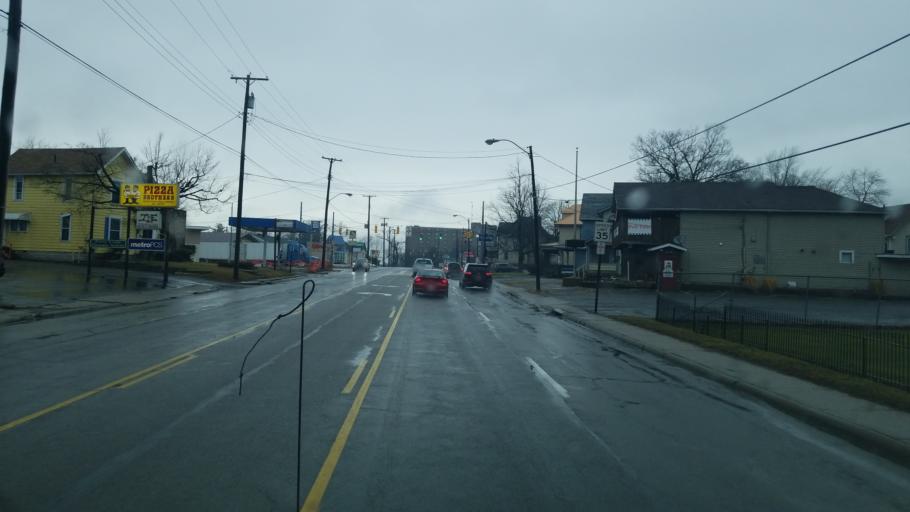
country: US
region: Ohio
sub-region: Marion County
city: Marion
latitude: 40.5782
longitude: -83.1260
